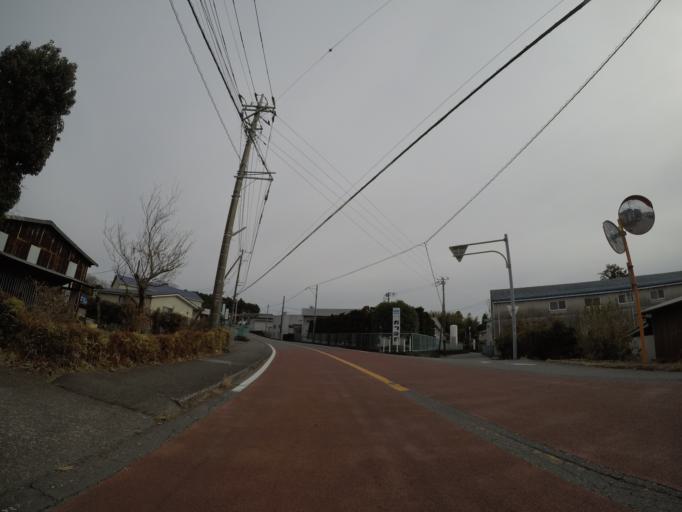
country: JP
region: Shizuoka
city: Fuji
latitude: 35.2124
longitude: 138.6755
